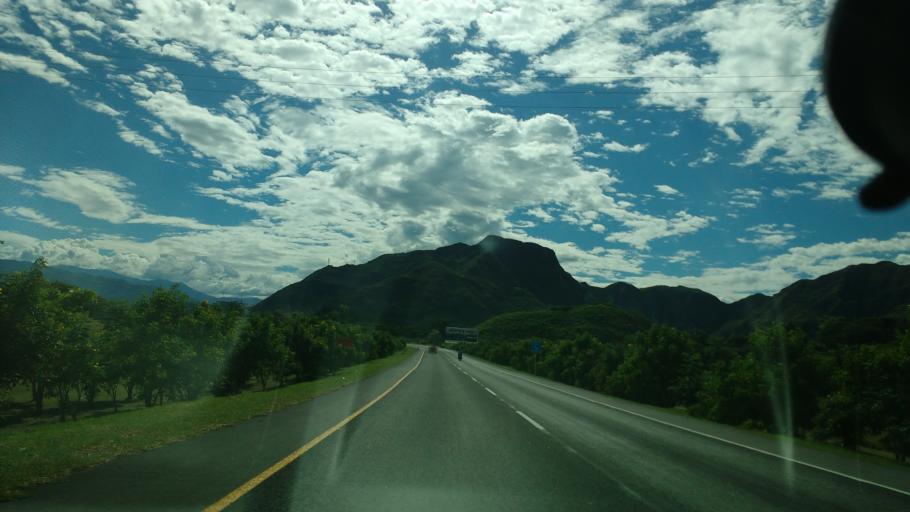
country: CO
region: Tolima
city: Valle de San Juan
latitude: 4.2761
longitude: -75.0051
